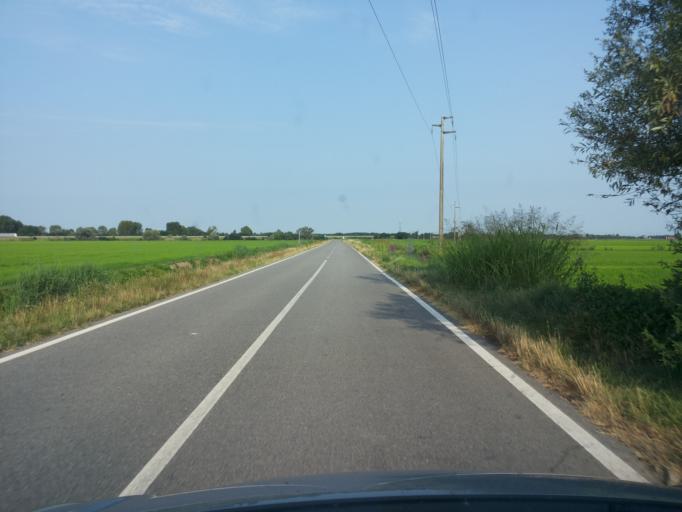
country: IT
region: Piedmont
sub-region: Provincia di Vercelli
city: Asigliano Vercellese
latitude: 45.2638
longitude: 8.4403
